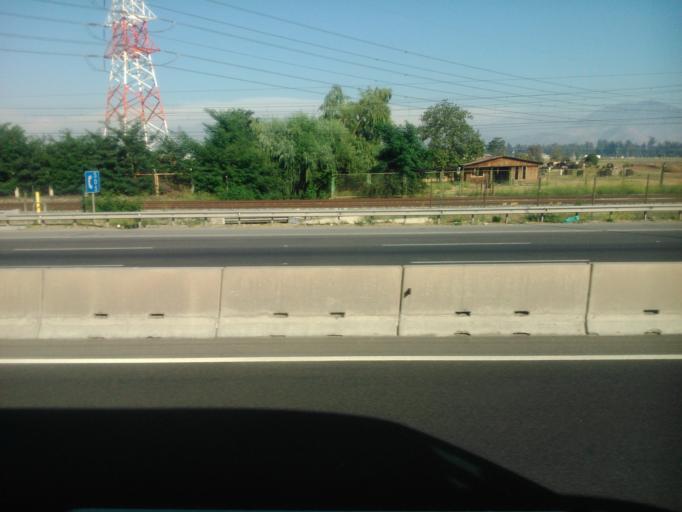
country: CL
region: Santiago Metropolitan
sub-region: Provincia de Maipo
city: San Bernardo
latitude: -33.6523
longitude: -70.7138
